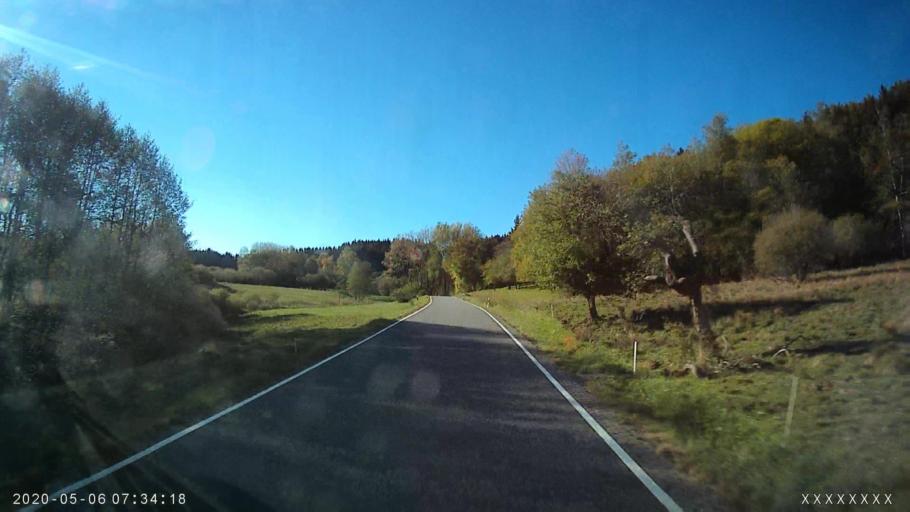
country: DE
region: Hesse
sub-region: Regierungsbezirk Giessen
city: Haiger
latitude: 50.8227
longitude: 8.2449
